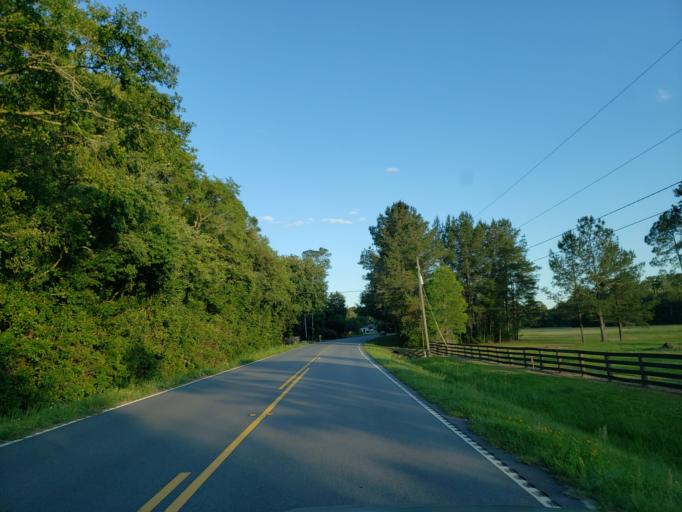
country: US
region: Georgia
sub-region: Lowndes County
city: Valdosta
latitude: 30.7594
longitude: -83.2605
